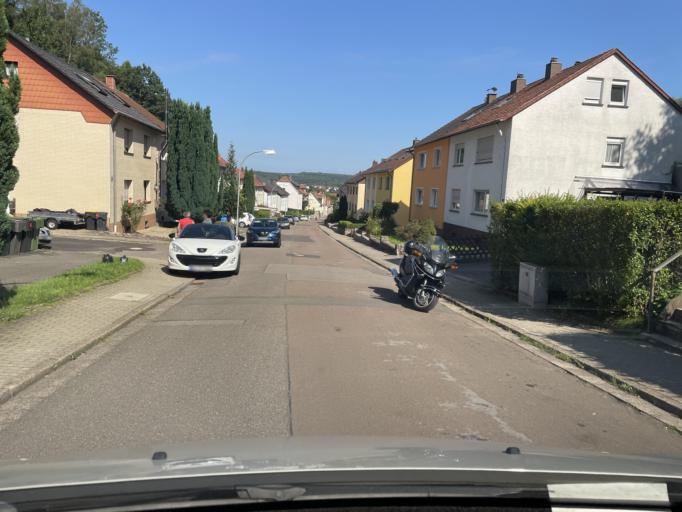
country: DE
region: Saarland
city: Sulzbach
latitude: 49.2649
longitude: 7.0386
